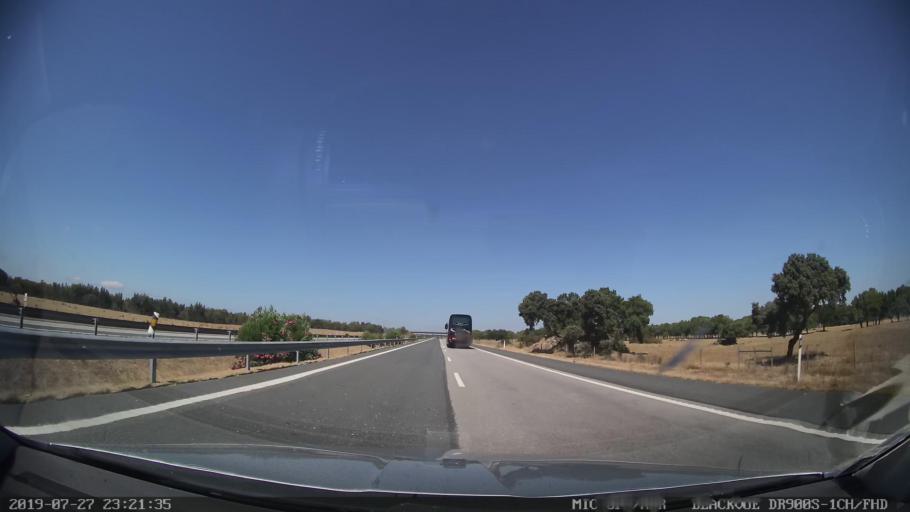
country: PT
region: Evora
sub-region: Evora
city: Evora
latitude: 38.6288
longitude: -7.9251
